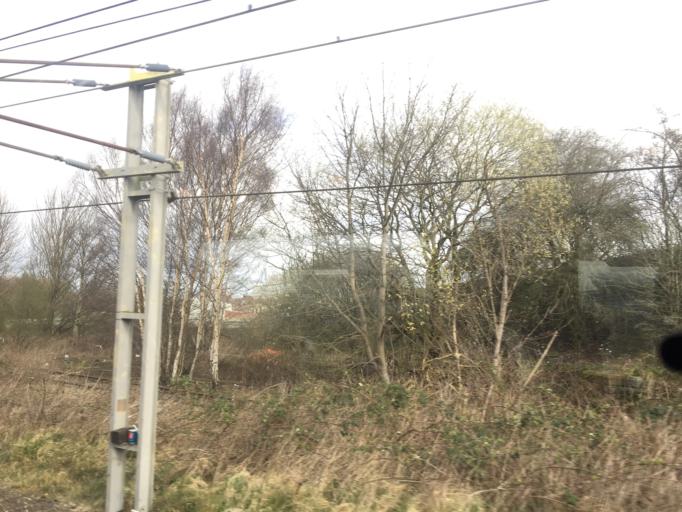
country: GB
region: England
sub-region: Cumbria
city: Carlisle
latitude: 54.8851
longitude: -2.9263
